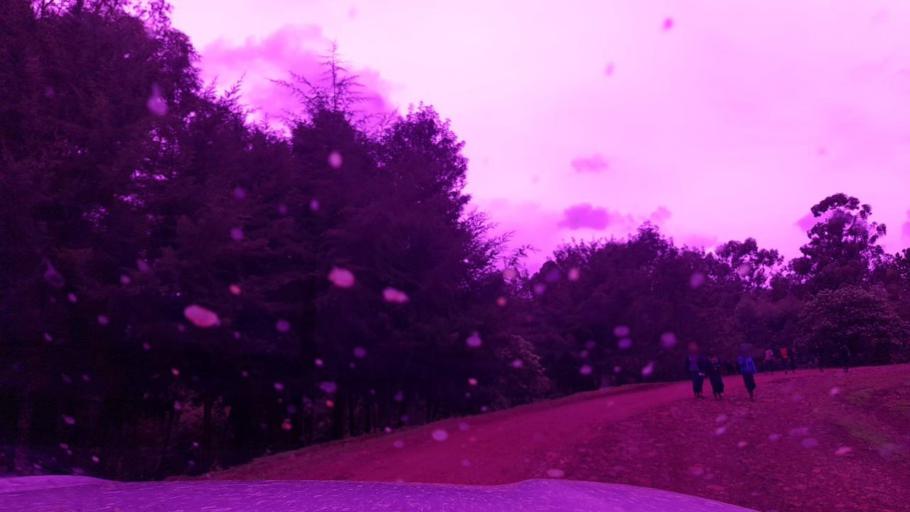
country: ET
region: Southern Nations, Nationalities, and People's Region
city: Tippi
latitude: 7.5715
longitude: 35.6630
